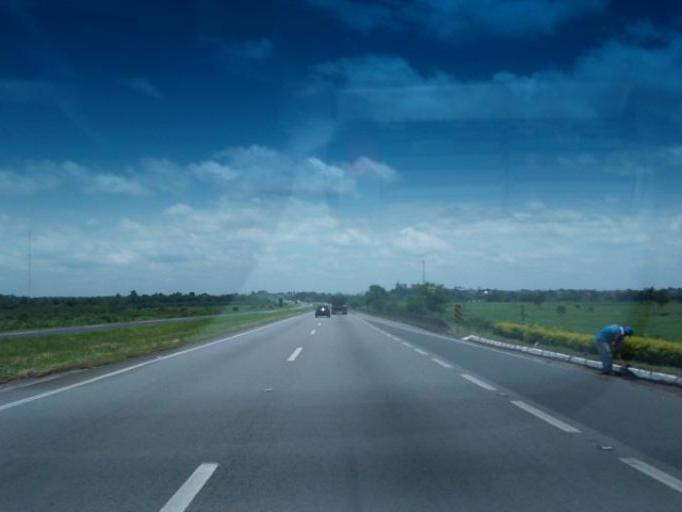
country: BR
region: Sao Paulo
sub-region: Registro
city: Registro
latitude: -24.4783
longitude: -47.8292
